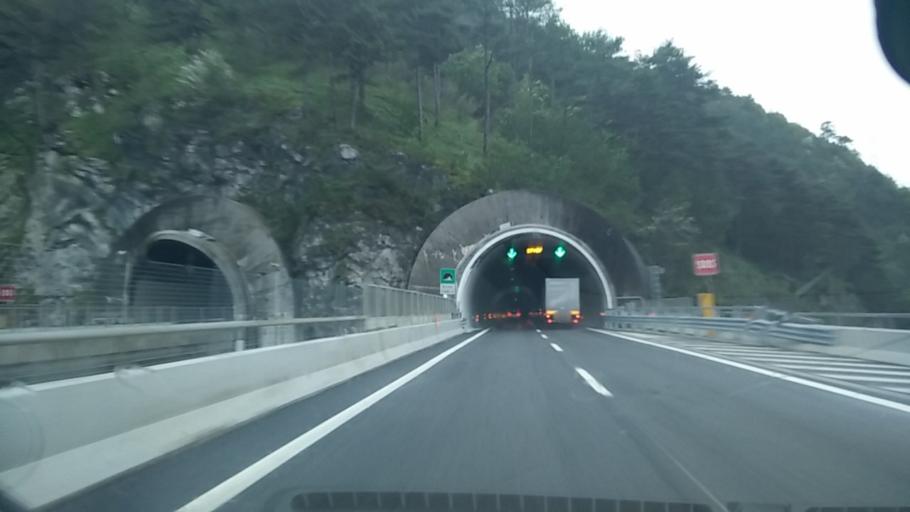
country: IT
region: Friuli Venezia Giulia
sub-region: Provincia di Udine
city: Chiusaforte
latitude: 46.4197
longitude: 13.3197
